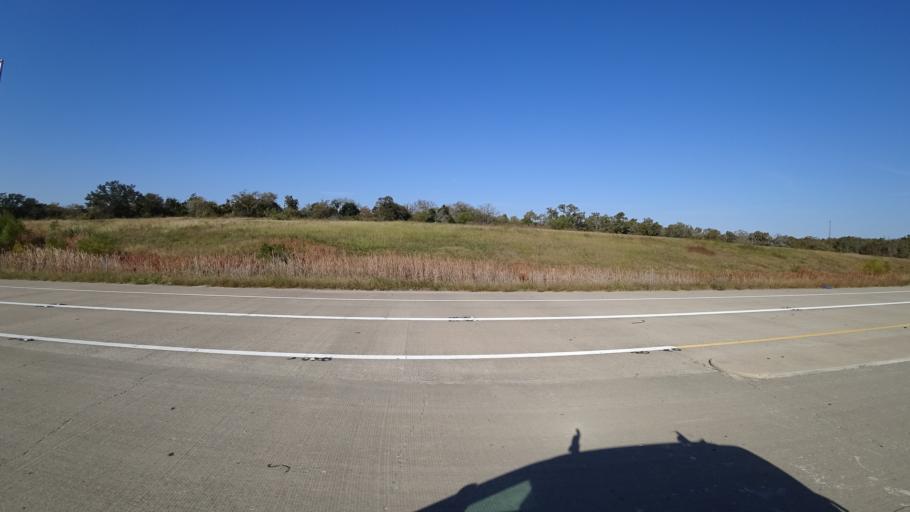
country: US
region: Texas
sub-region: Travis County
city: Hornsby Bend
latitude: 30.2654
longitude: -97.5973
